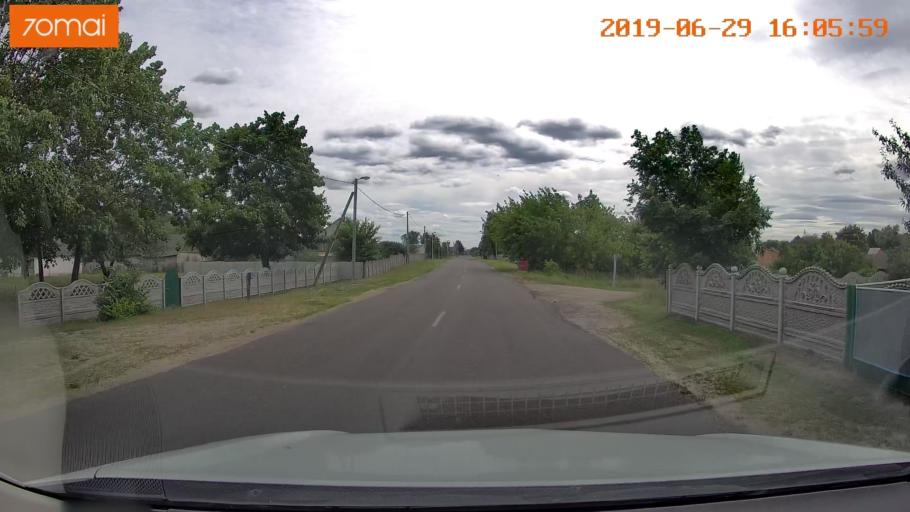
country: BY
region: Brest
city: Luninyets
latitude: 52.2123
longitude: 27.0157
